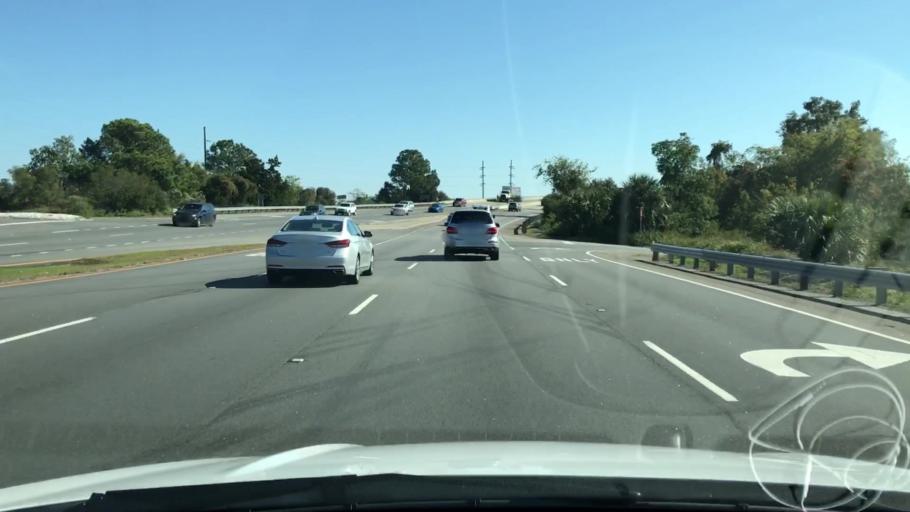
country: US
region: South Carolina
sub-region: Beaufort County
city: Hilton Head Island
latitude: 32.2286
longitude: -80.7864
